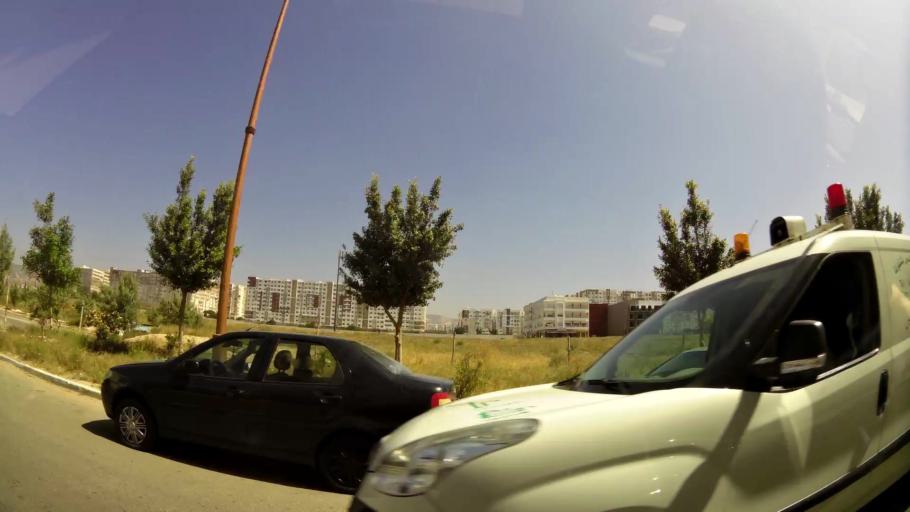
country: MA
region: Oued ed Dahab-Lagouira
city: Dakhla
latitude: 30.4319
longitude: -9.5637
